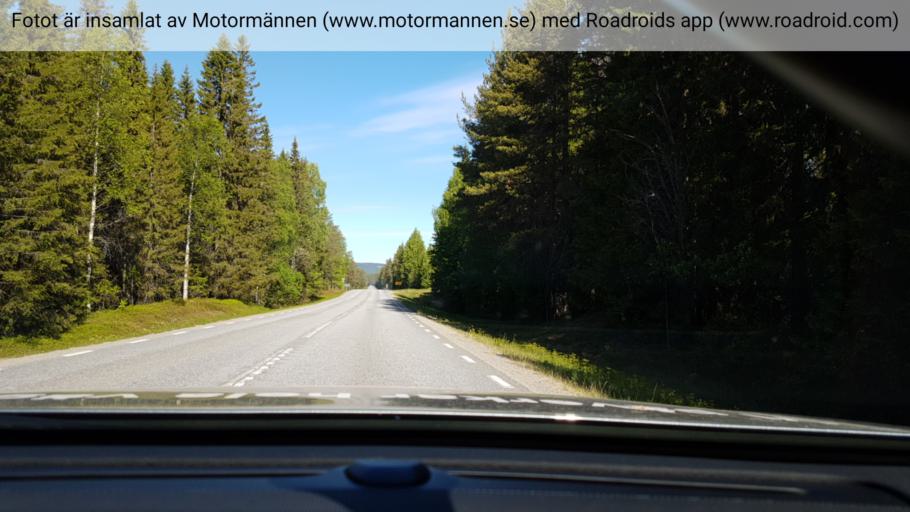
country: SE
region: Vaesterbotten
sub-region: Bjurholms Kommun
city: Bjurholm
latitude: 63.9619
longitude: 18.8533
